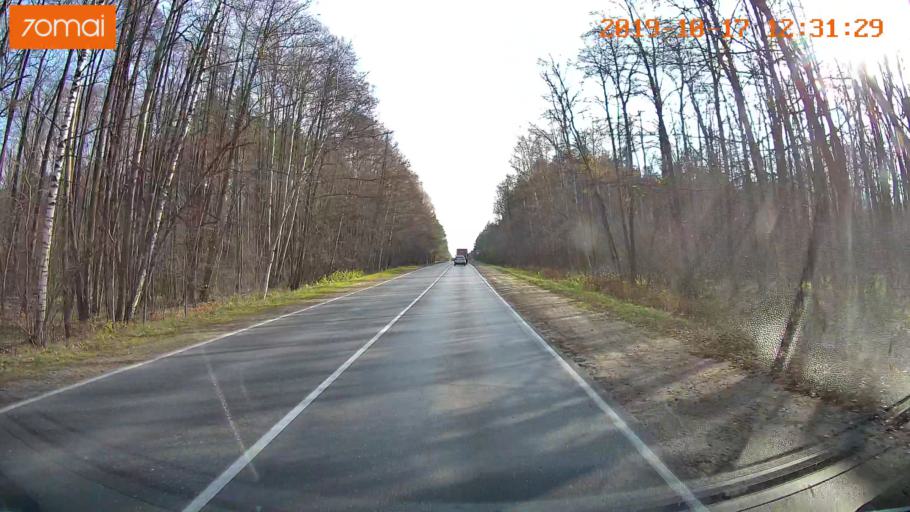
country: RU
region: Rjazan
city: Syntul
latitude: 54.9678
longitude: 41.3344
